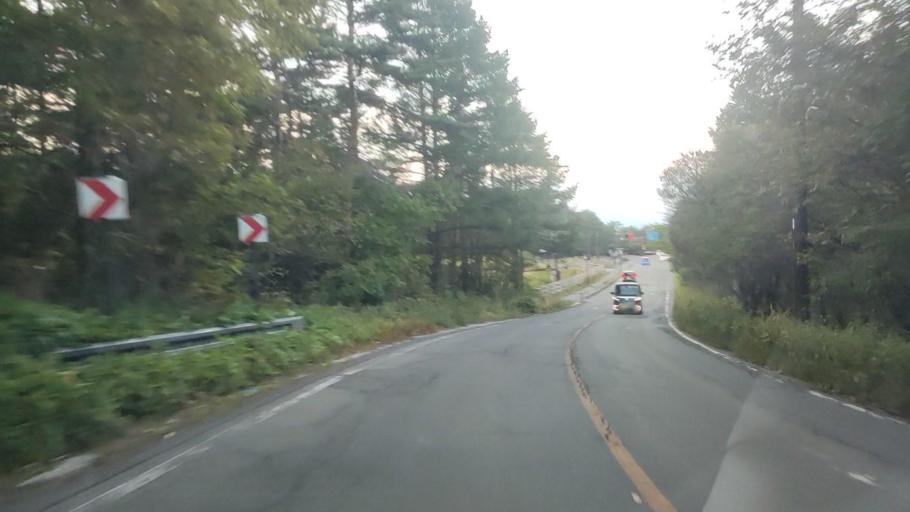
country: JP
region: Nagano
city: Komoro
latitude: 36.4277
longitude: 138.5710
